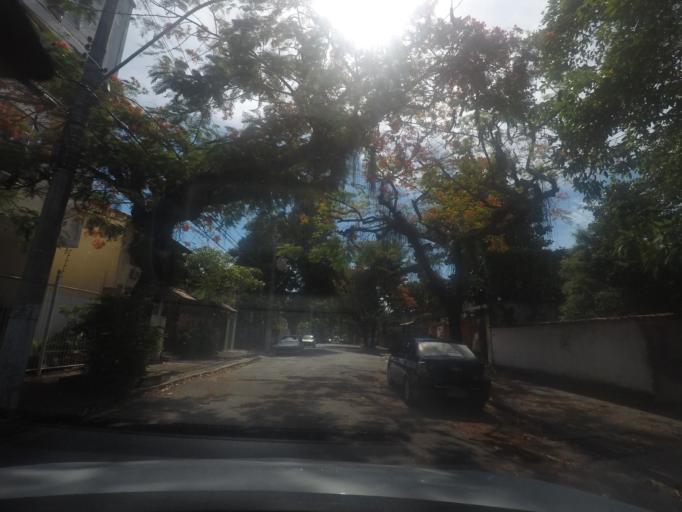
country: BR
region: Rio de Janeiro
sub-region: Niteroi
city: Niteroi
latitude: -22.9171
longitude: -43.0911
